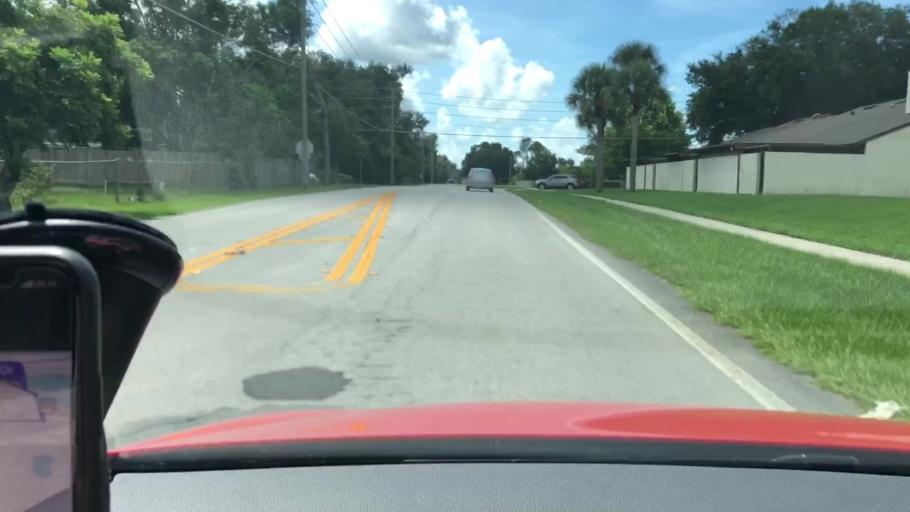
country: US
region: Florida
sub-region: Lake County
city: Eustis
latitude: 28.8483
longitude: -81.6546
